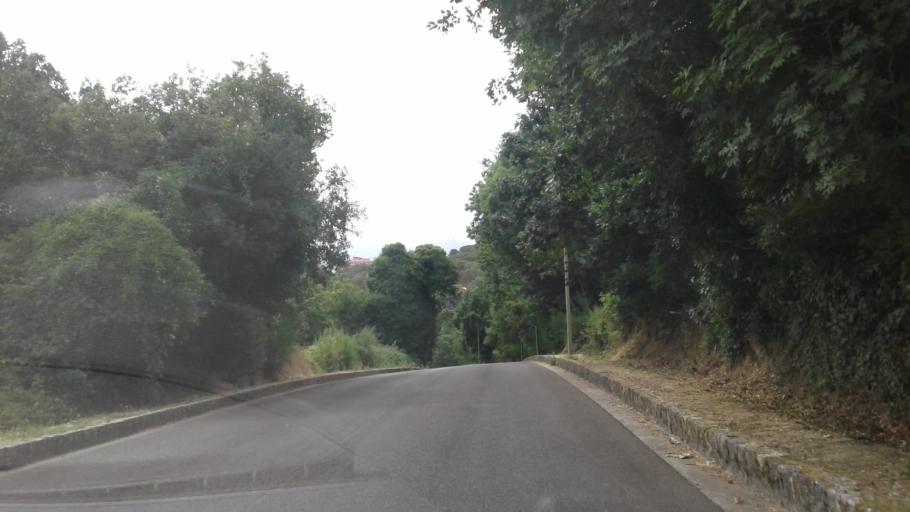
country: IT
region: Sardinia
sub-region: Provincia di Olbia-Tempio
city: Tempio Pausania
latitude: 40.9012
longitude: 9.0937
